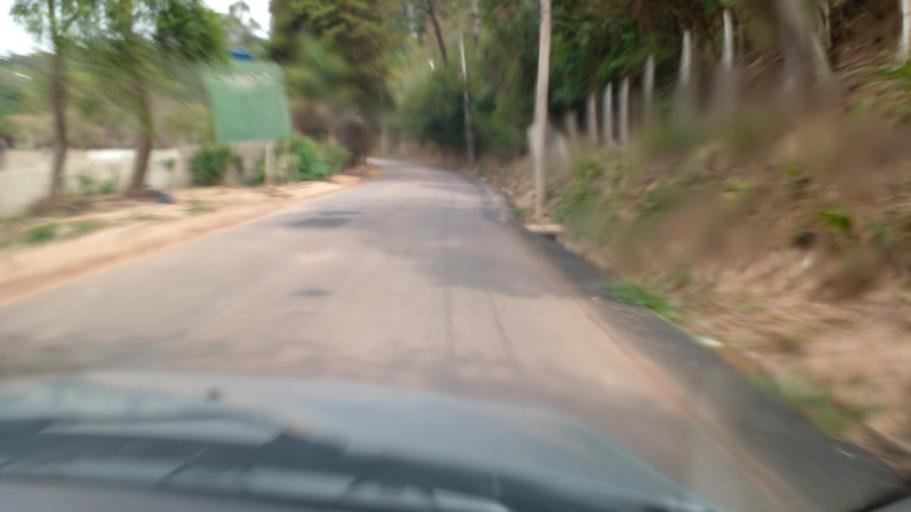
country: BR
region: Sao Paulo
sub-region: Jundiai
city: Jundiai
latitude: -23.1292
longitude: -46.8917
